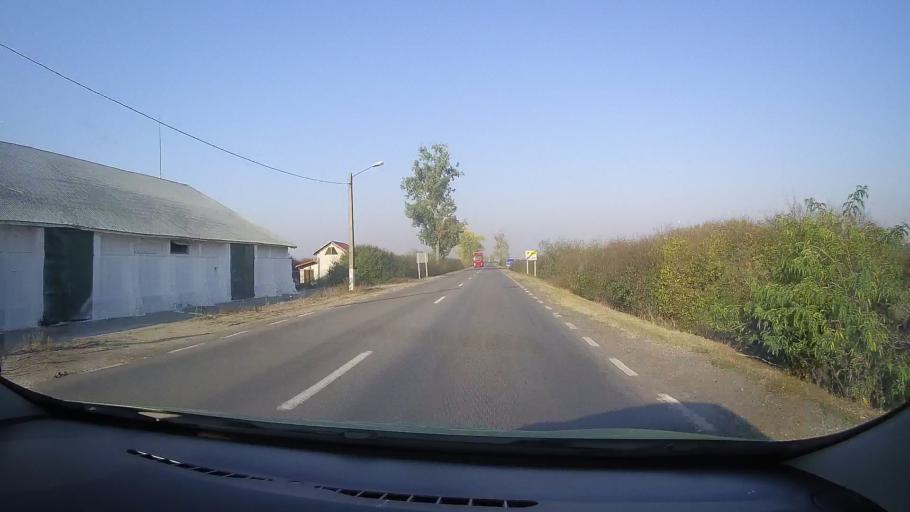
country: RO
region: Arad
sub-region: Comuna Socodor
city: Socodor
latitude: 46.5016
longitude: 21.4285
